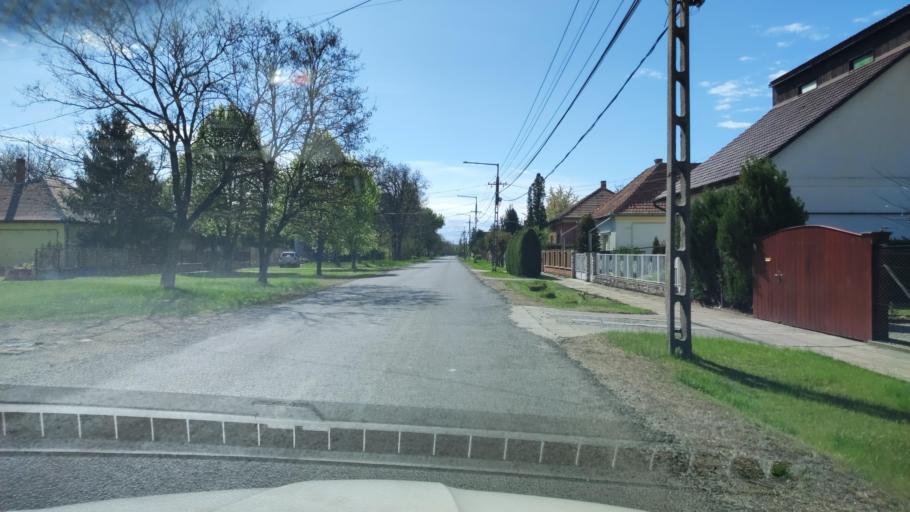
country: HU
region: Pest
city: Abony
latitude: 47.1786
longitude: 20.0124
